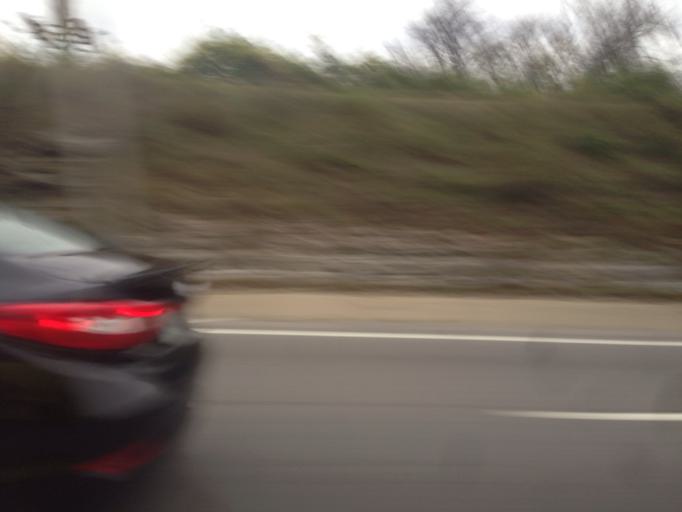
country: US
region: Tennessee
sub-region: Davidson County
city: Nashville
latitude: 36.1431
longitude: -86.7367
